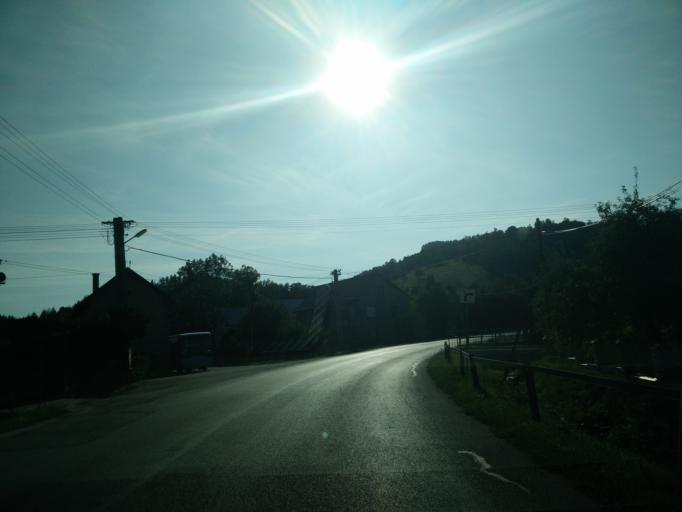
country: SK
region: Nitriansky
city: Prievidza
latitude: 48.8788
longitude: 18.7250
